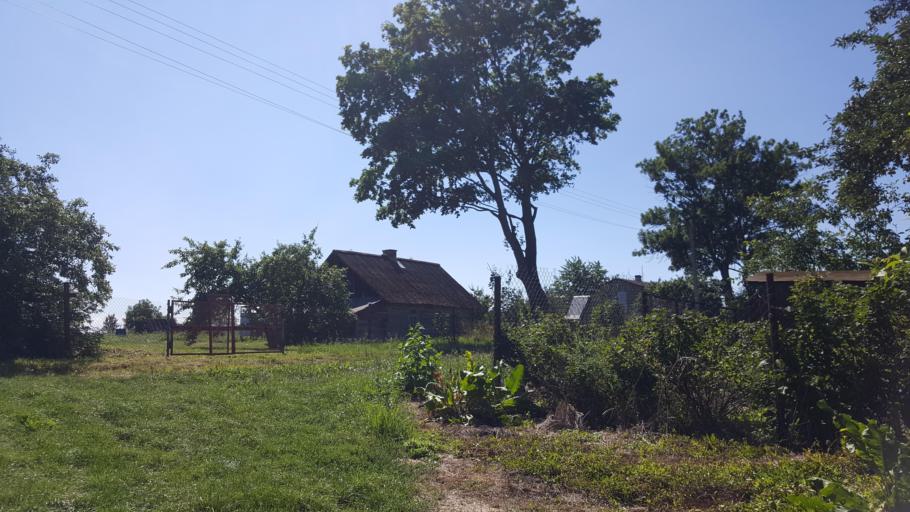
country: BY
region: Brest
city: Charnawchytsy
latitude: 52.2109
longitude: 23.7880
